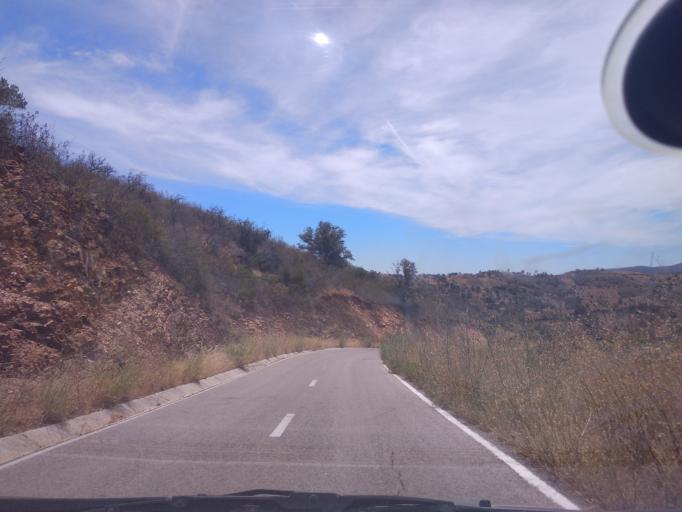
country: PT
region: Faro
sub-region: Sao Bras de Alportel
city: Sao Bras de Alportel
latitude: 37.1858
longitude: -7.7973
